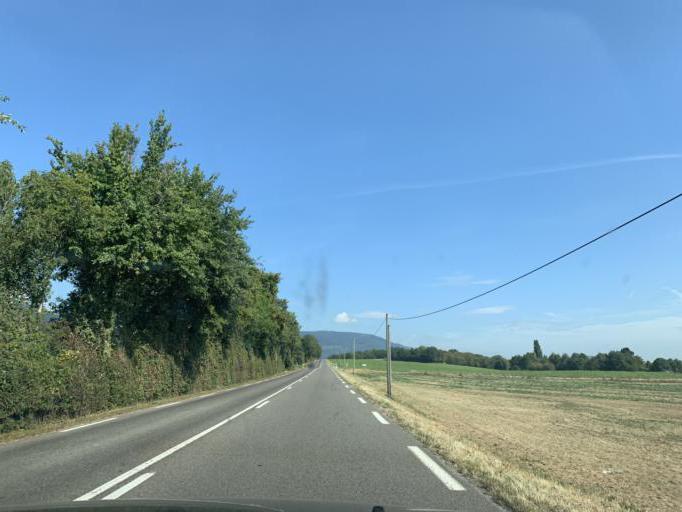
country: FR
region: Rhone-Alpes
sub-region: Departement de l'Ain
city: Chevry
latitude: 46.2926
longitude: 6.0420
